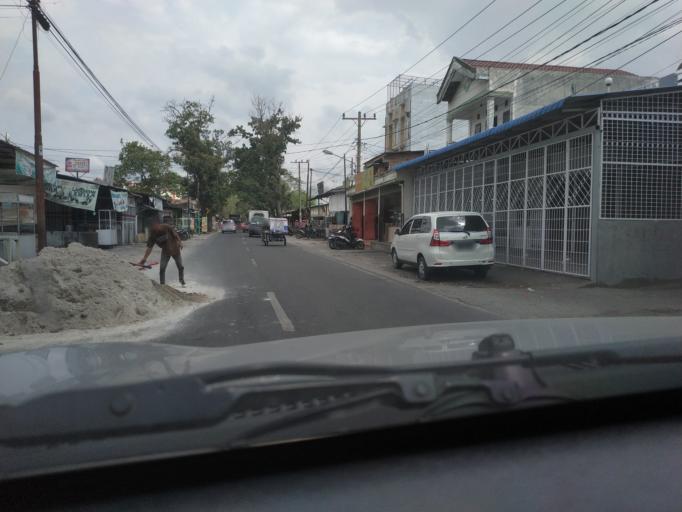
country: ID
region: North Sumatra
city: Sunggal
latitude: 3.5846
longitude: 98.6323
